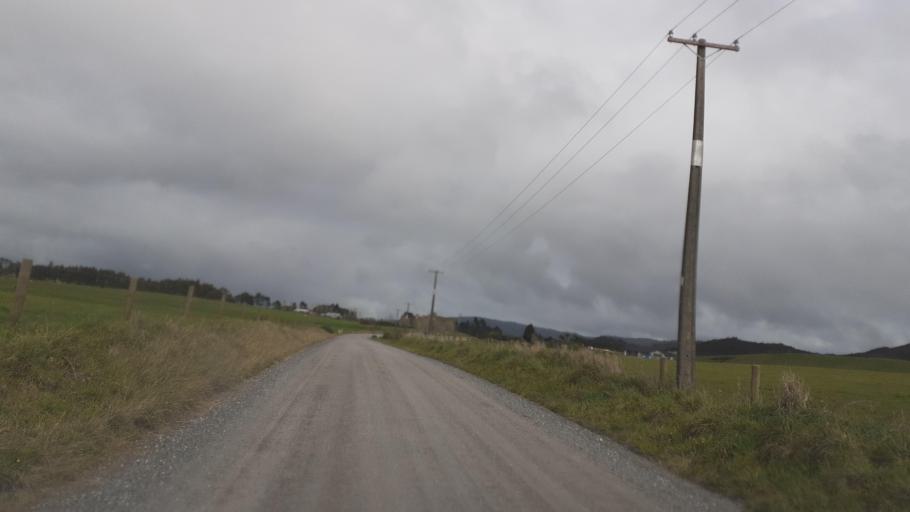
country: NZ
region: Northland
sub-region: Far North District
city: Waimate North
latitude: -35.2434
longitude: 173.8053
